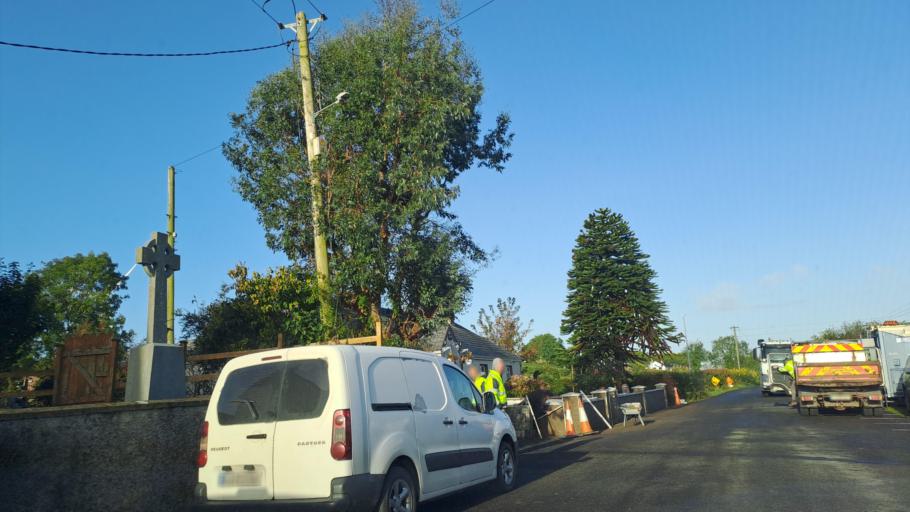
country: IE
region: Ulster
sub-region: County Monaghan
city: Castleblayney
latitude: 54.0857
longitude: -6.8615
